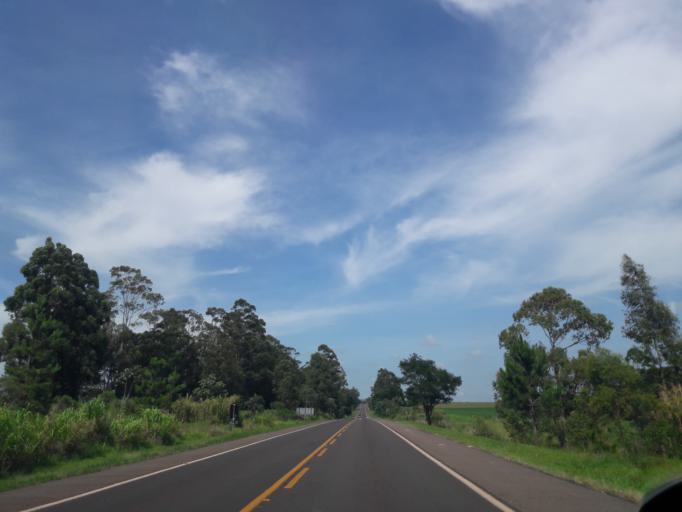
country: BR
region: Parana
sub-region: Campo Mourao
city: Campo Mourao
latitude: -24.2780
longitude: -52.5252
